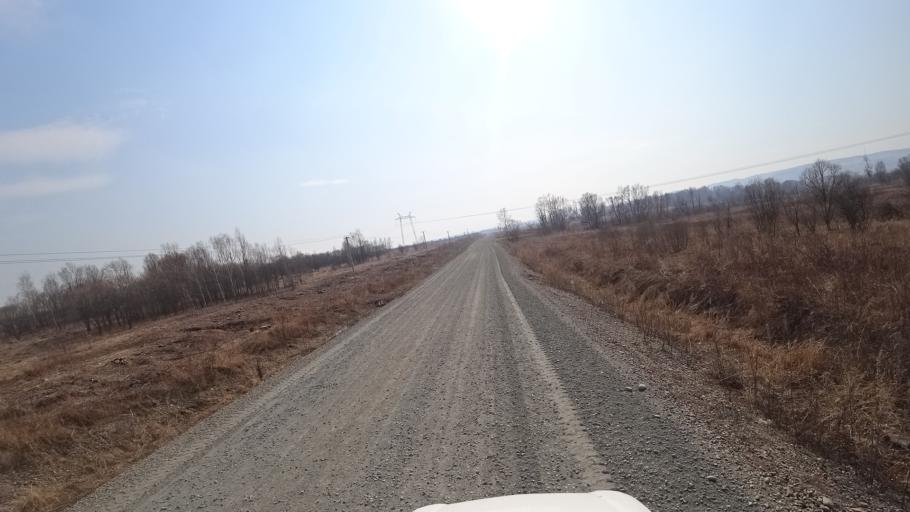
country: RU
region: Amur
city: Novobureyskiy
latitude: 49.8168
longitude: 129.9772
